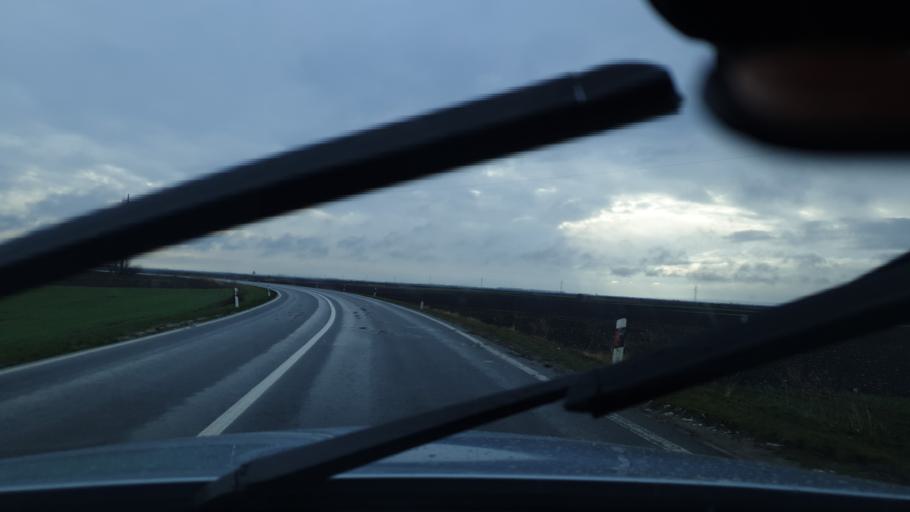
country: RS
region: Autonomna Pokrajina Vojvodina
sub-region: Juznobanatski Okrug
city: Kovin
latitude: 44.8113
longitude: 20.8578
